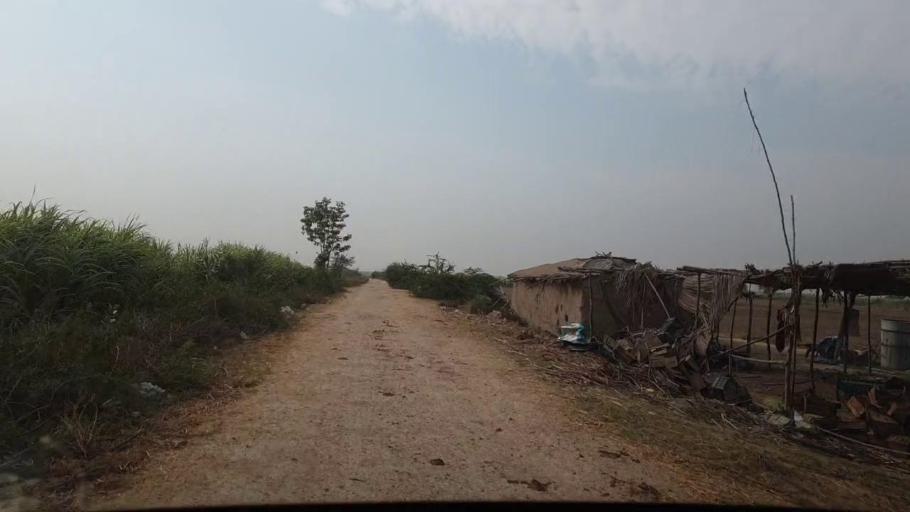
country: PK
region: Sindh
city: Chuhar Jamali
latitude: 24.4149
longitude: 67.9392
